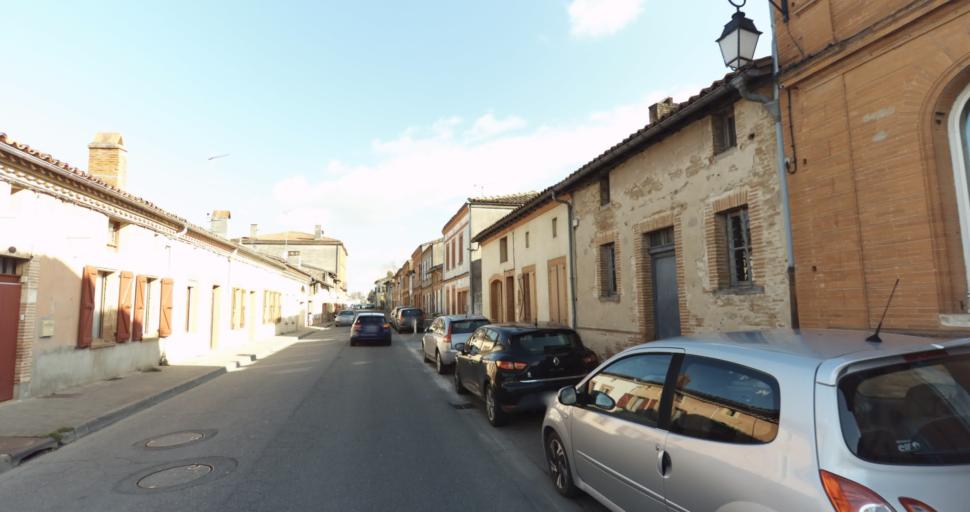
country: FR
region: Midi-Pyrenees
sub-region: Departement de la Haute-Garonne
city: Auterive
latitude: 43.3518
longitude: 1.4811
